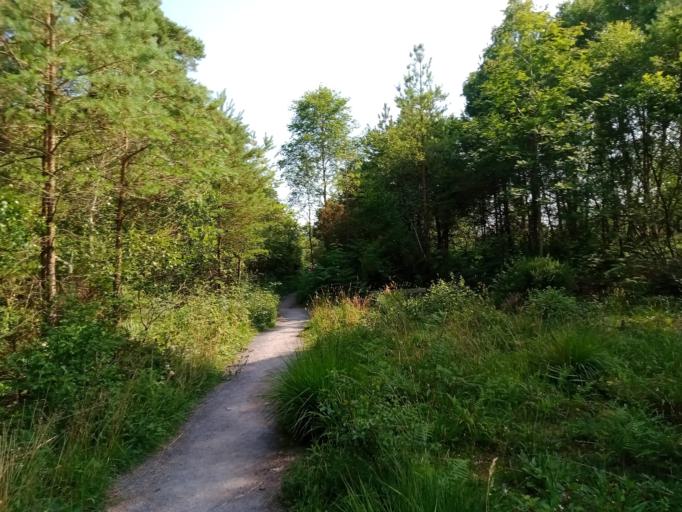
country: IE
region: Leinster
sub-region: Laois
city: Abbeyleix
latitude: 52.8967
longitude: -7.3570
